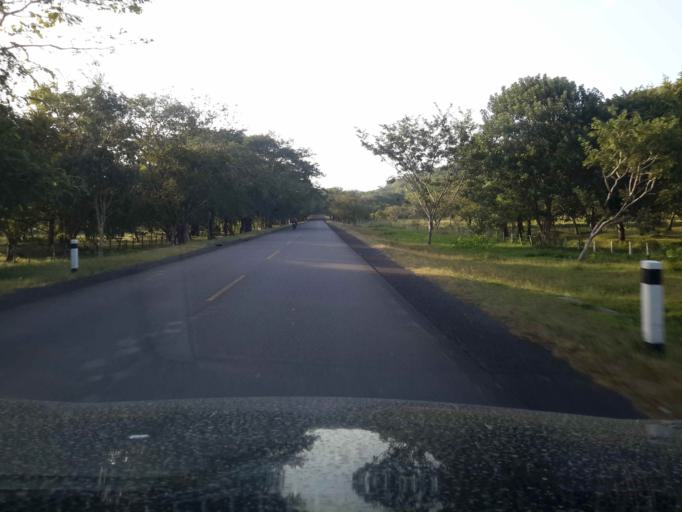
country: NI
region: Rio San Juan
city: San Miguelito
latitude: 11.3990
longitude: -84.8240
